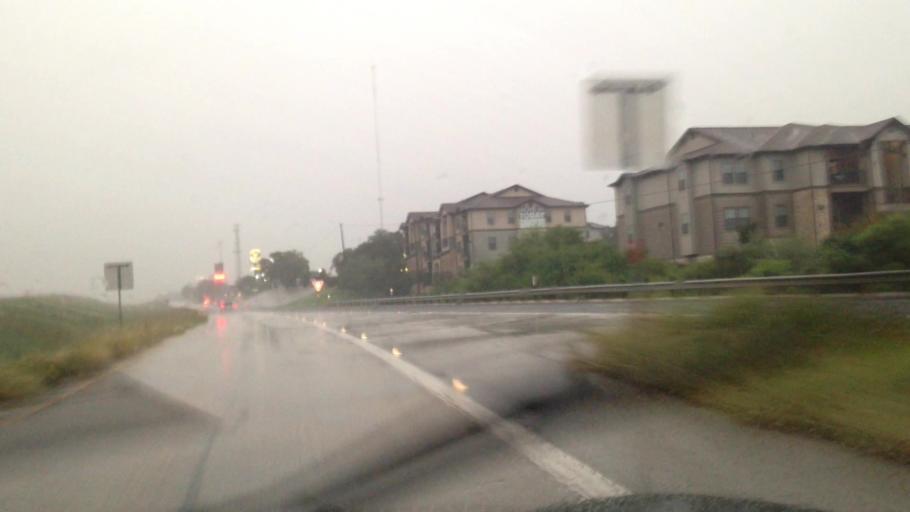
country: US
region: Texas
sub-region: Bexar County
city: Live Oak
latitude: 29.6018
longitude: -98.3915
